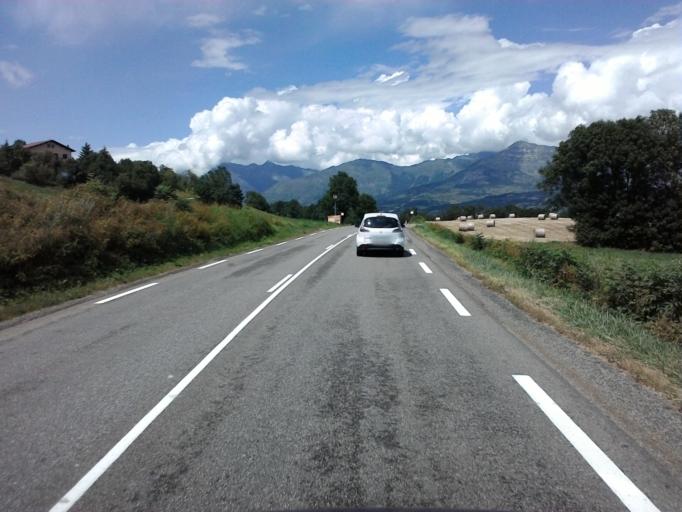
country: FR
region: Provence-Alpes-Cote d'Azur
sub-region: Departement des Hautes-Alpes
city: Gap
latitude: 44.6239
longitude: 6.0828
